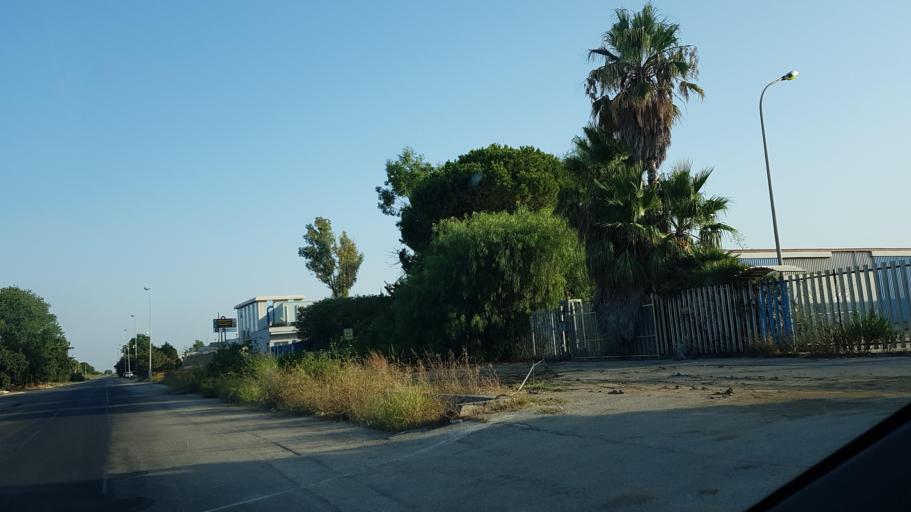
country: IT
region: Apulia
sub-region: Provincia di Brindisi
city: Materdomini
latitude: 40.6322
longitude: 17.9740
